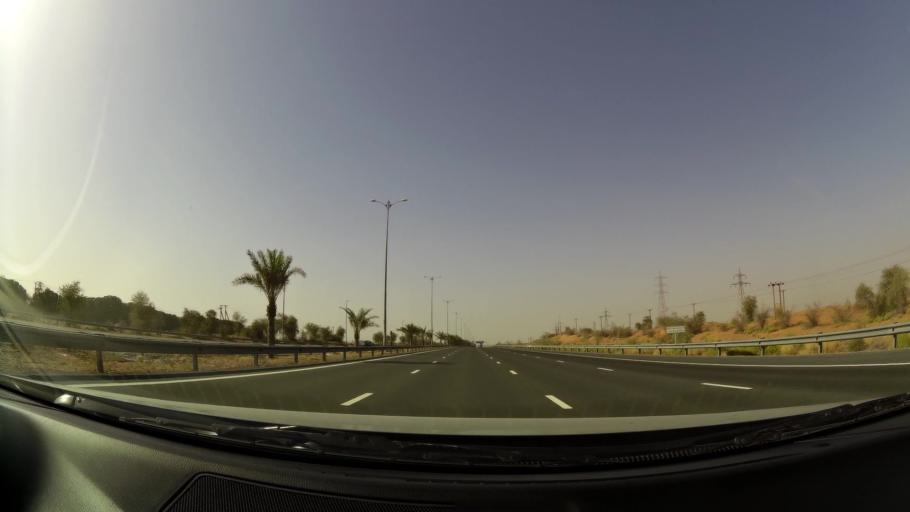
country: OM
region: Al Buraimi
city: Al Buraymi
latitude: 24.4492
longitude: 55.7839
